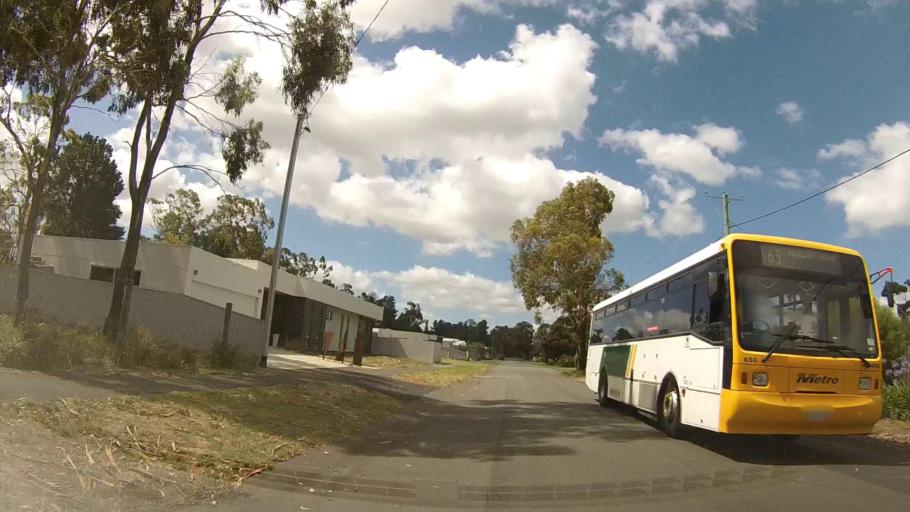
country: AU
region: Tasmania
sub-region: Clarence
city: Seven Mile Beach
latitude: -42.8578
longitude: 147.5022
